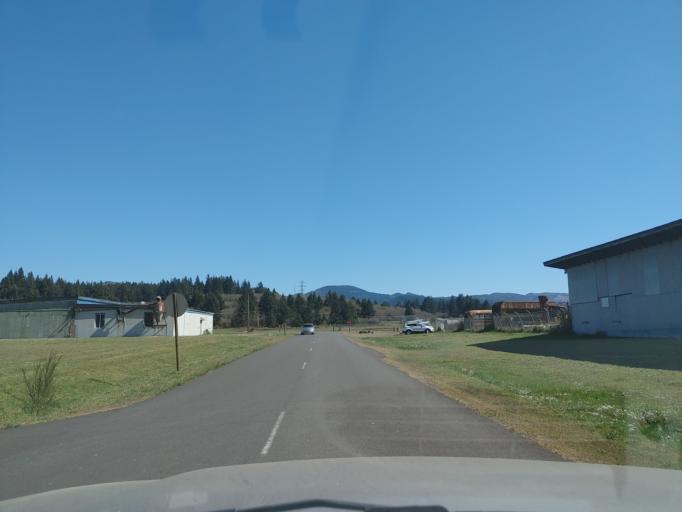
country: US
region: Oregon
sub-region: Tillamook County
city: Tillamook
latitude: 45.4193
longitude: -123.8029
